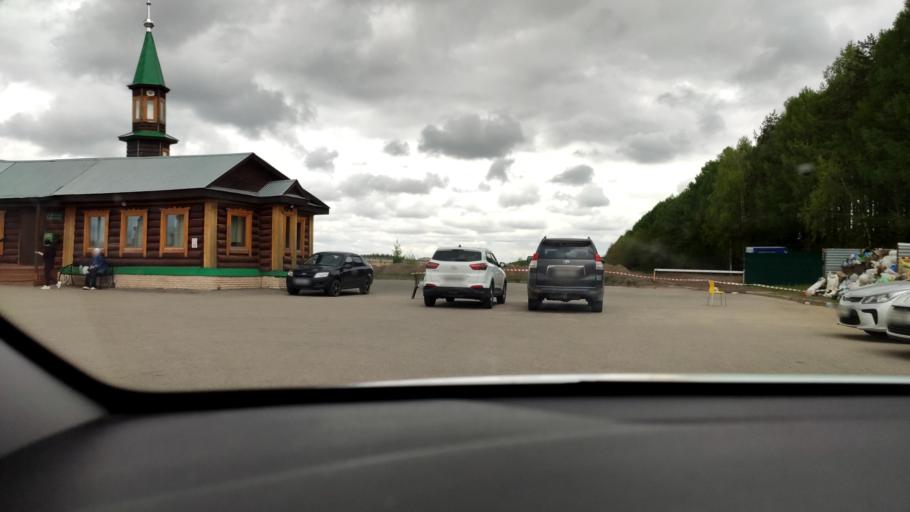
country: RU
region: Tatarstan
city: Vysokaya Gora
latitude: 55.8009
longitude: 49.3270
